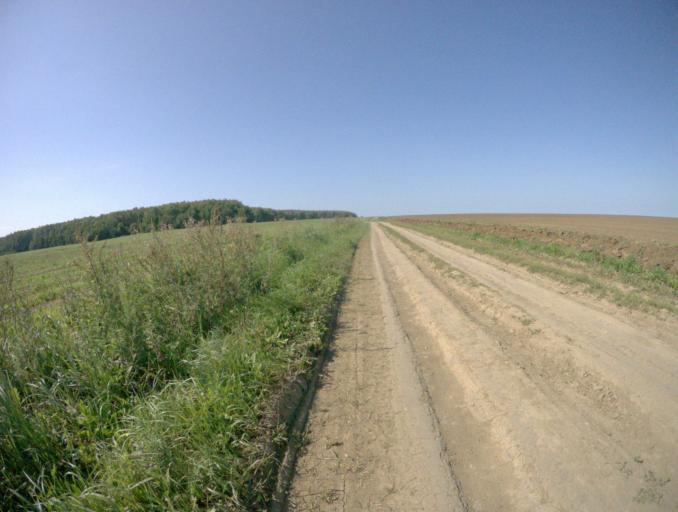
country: RU
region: Vladimir
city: Bogolyubovo
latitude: 56.2454
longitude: 40.4472
